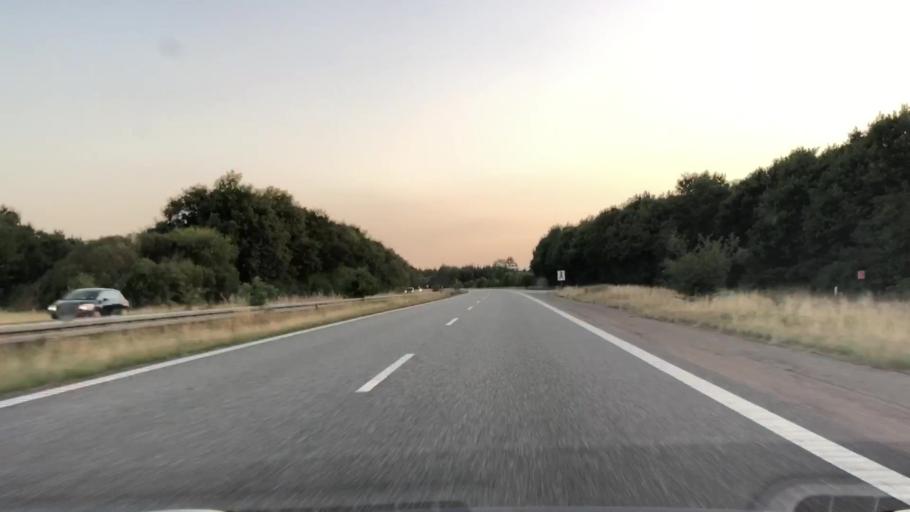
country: DK
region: South Denmark
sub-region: Aabenraa Kommune
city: Padborg
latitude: 54.8297
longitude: 9.3315
